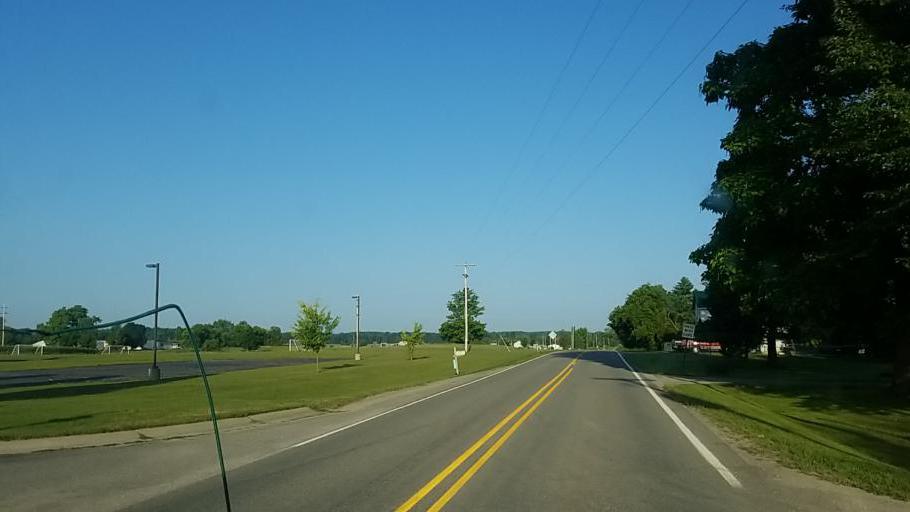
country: US
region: Michigan
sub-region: Montcalm County
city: Howard City
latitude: 43.3666
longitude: -85.4798
